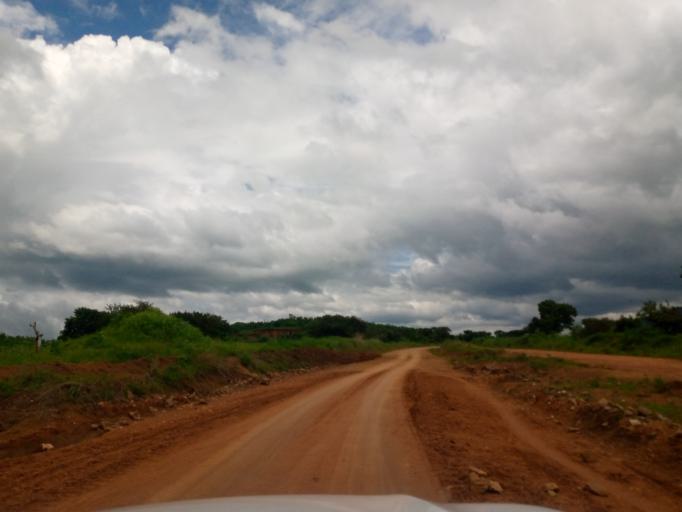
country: ET
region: Oromiya
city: Mendi
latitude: 10.1956
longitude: 35.0921
